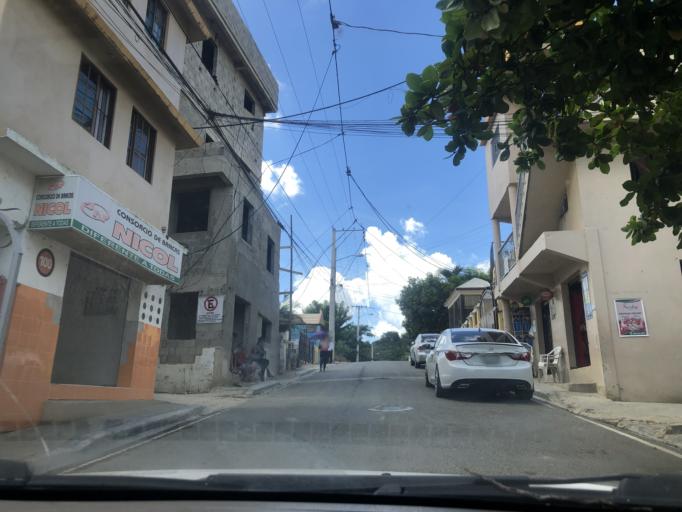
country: DO
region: Santiago
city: Santiago de los Caballeros
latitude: 19.4099
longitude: -70.7043
